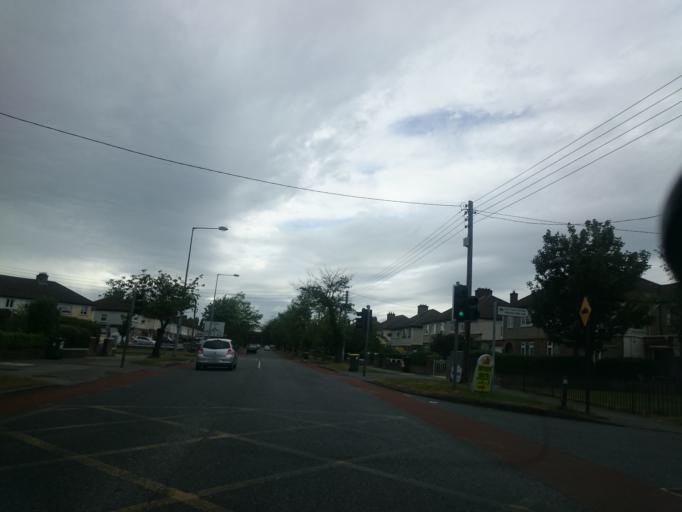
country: IE
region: Leinster
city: Templeogue
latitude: 53.3015
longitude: -6.3052
